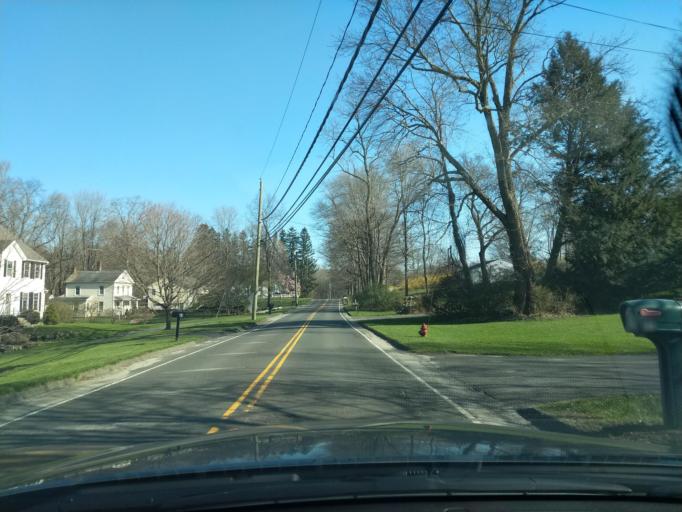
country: US
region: Connecticut
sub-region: Fairfield County
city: Newtown
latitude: 41.4043
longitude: -73.2964
